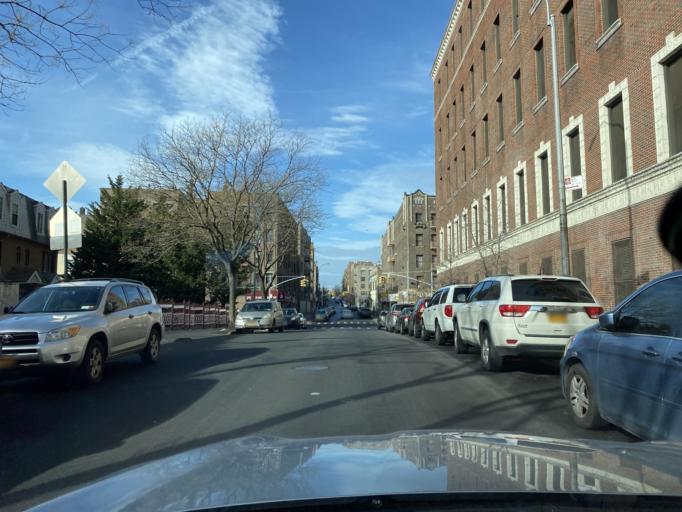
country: US
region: New York
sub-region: New York County
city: Inwood
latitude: 40.8585
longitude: -73.8967
